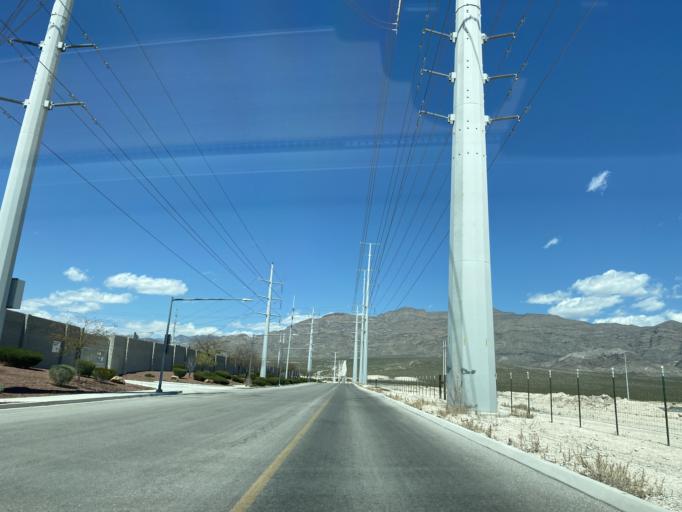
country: US
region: Nevada
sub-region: Clark County
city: North Las Vegas
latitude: 36.3217
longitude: -115.2071
